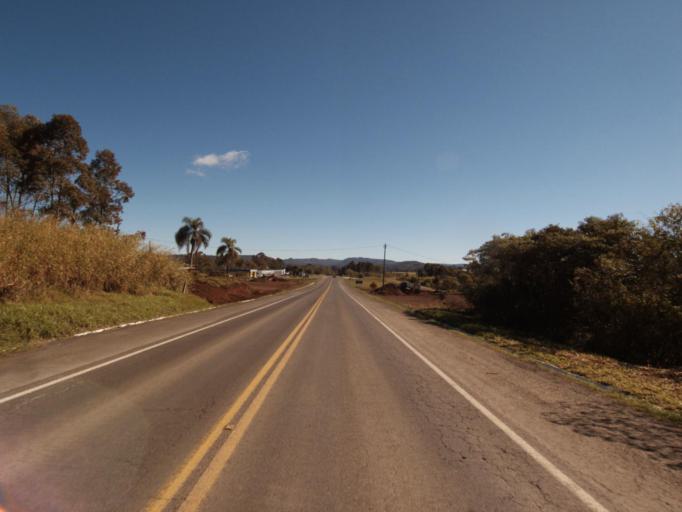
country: BR
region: Santa Catarina
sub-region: Joacaba
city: Joacaba
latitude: -27.1748
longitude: -51.5510
